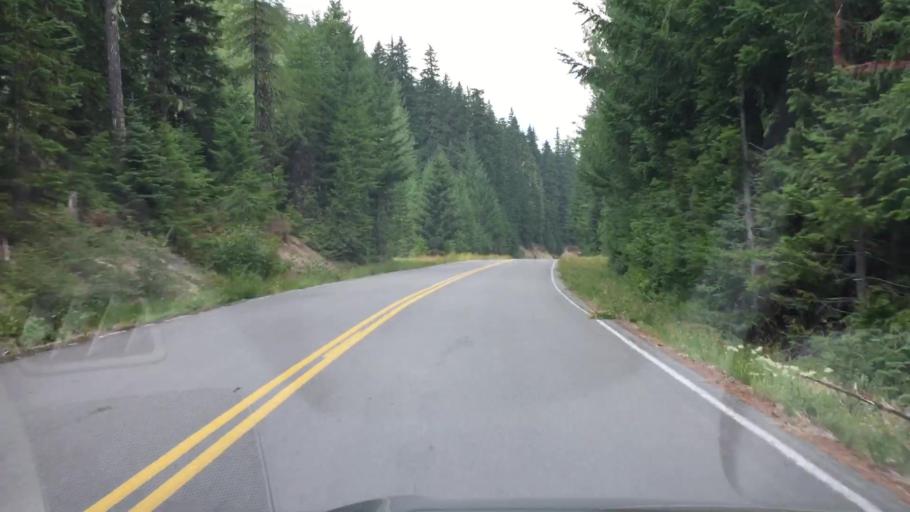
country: US
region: Washington
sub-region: Klickitat County
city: White Salmon
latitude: 46.1172
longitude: -121.6183
